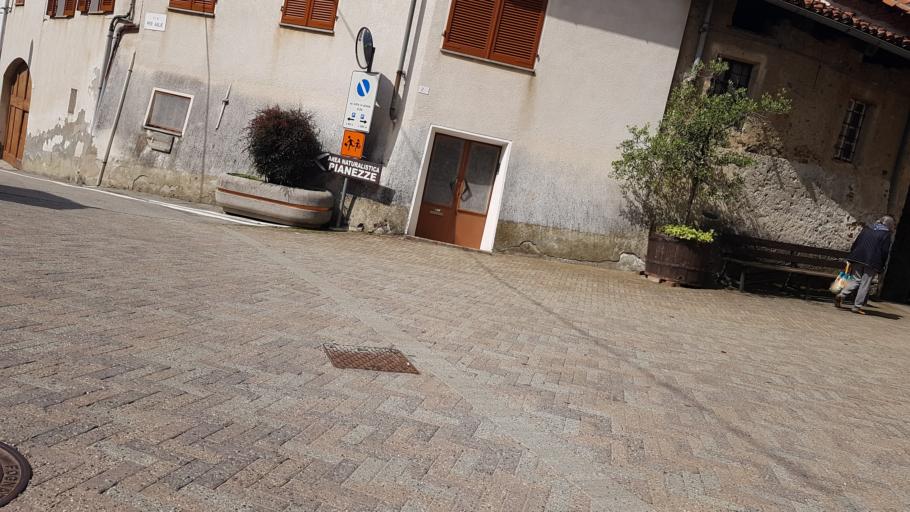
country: IT
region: Piedmont
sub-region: Provincia di Torino
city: Vialfre
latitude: 45.3813
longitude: 7.8171
